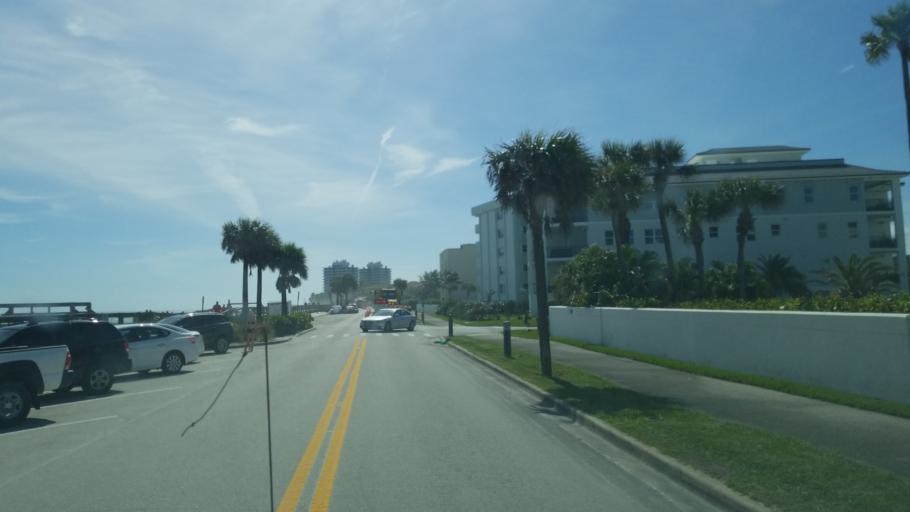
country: US
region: Florida
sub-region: Indian River County
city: Vero Beach
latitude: 27.6628
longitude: -80.3585
